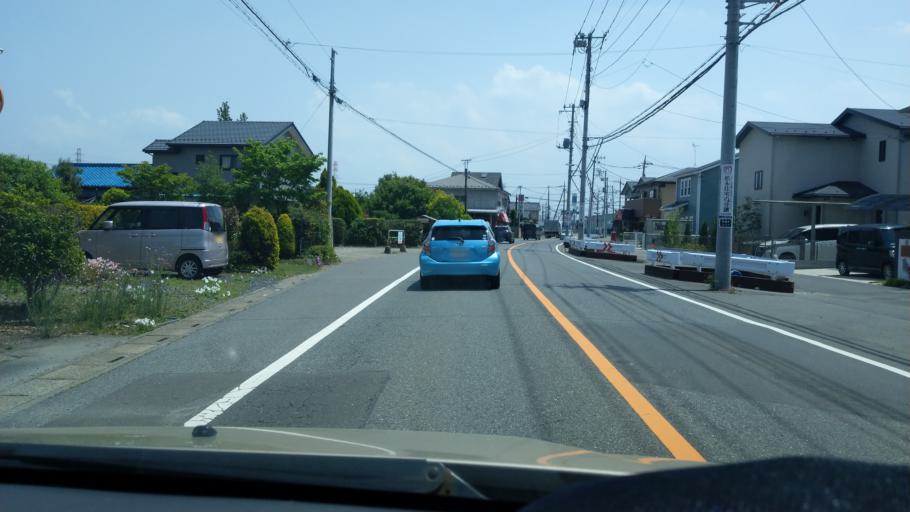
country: JP
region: Saitama
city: Koshigaya
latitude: 35.9083
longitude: 139.7281
